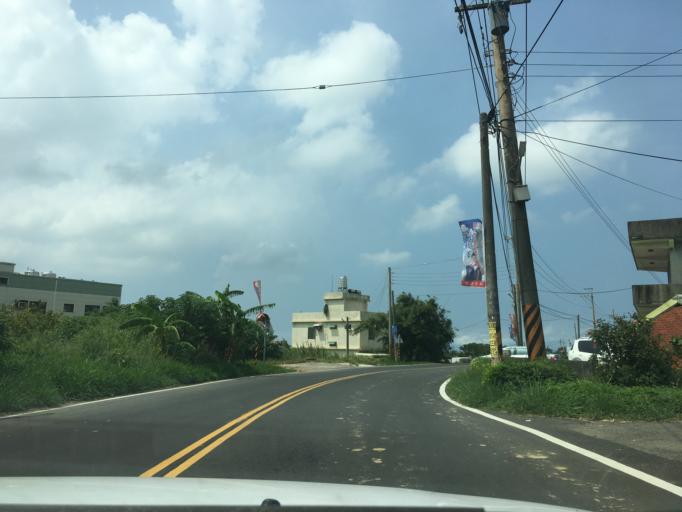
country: TW
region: Taiwan
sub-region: Hsinchu
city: Zhubei
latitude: 24.9096
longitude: 121.0087
